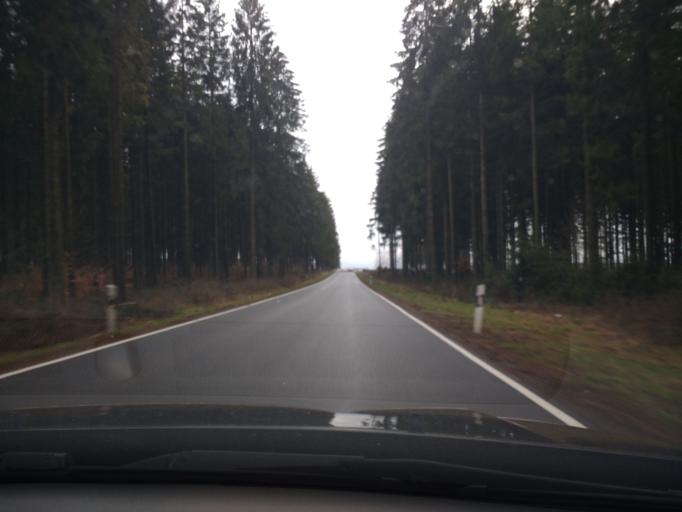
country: DE
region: Rheinland-Pfalz
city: Damflos
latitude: 49.6778
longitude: 6.9730
